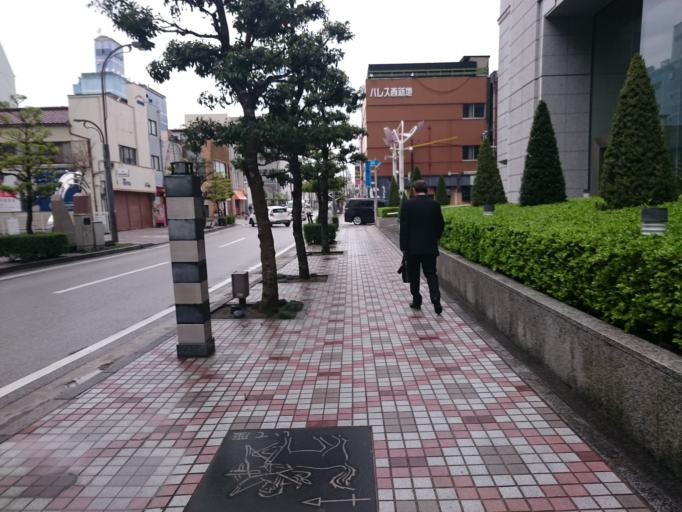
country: JP
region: Mie
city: Yokkaichi
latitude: 34.9692
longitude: 136.6205
